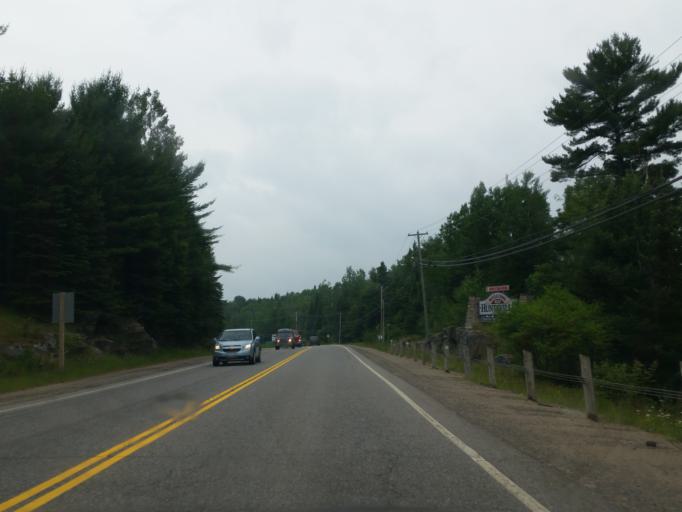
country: CA
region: Ontario
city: Huntsville
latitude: 45.3534
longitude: -79.1461
